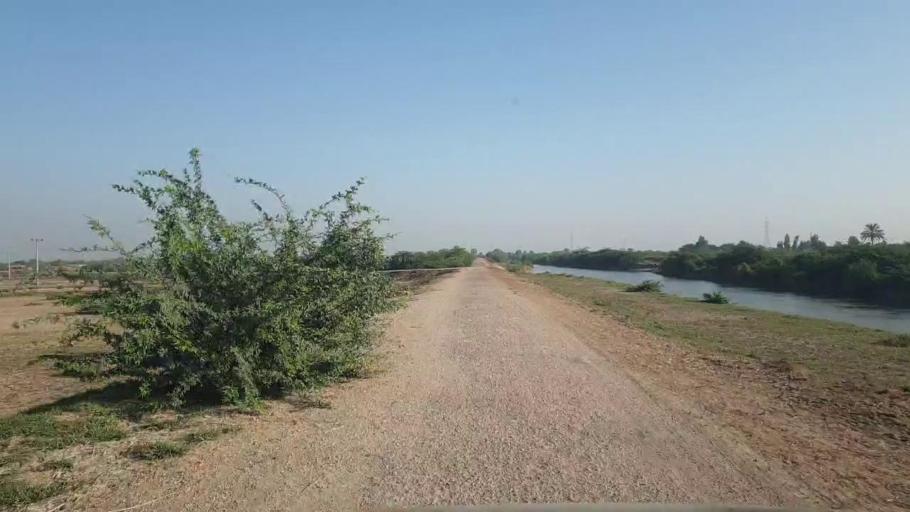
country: PK
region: Sindh
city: Badin
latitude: 24.6962
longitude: 68.8163
